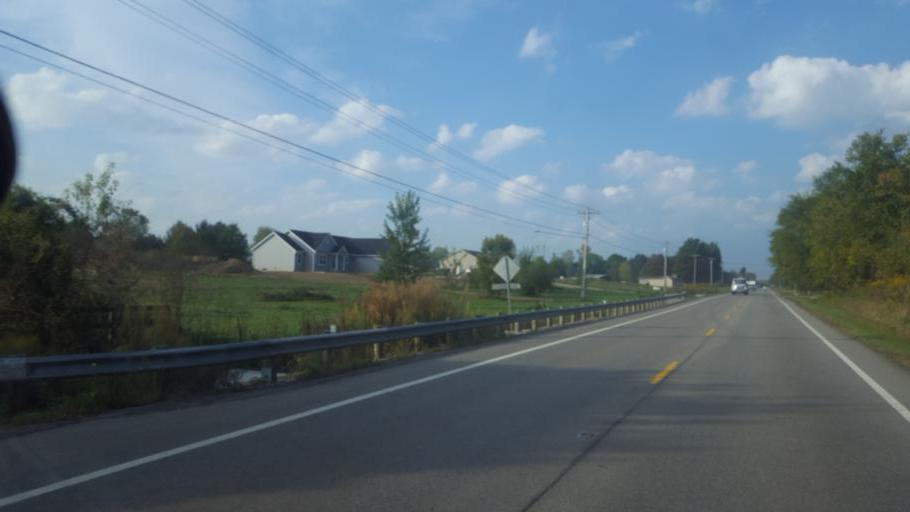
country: US
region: Ohio
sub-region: Licking County
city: Johnstown
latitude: 40.1967
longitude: -82.5924
